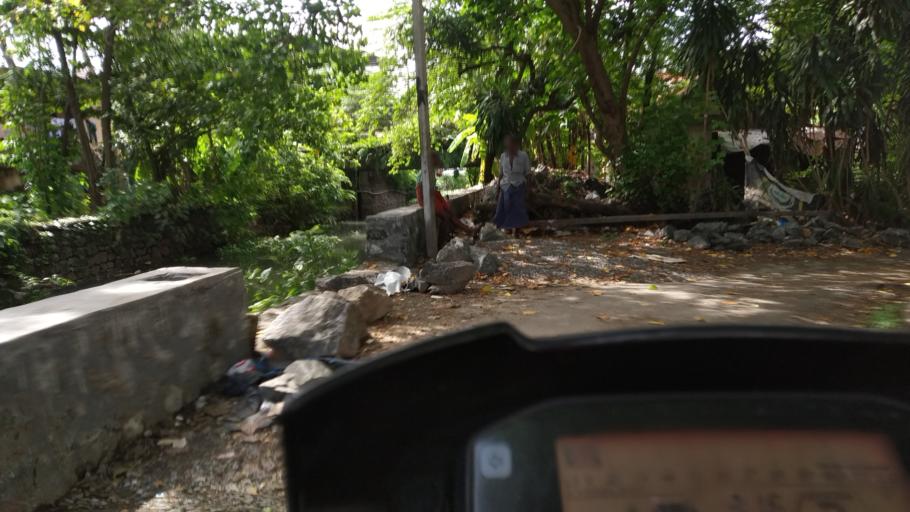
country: IN
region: Kerala
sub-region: Ernakulam
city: Cochin
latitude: 9.9826
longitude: 76.2913
